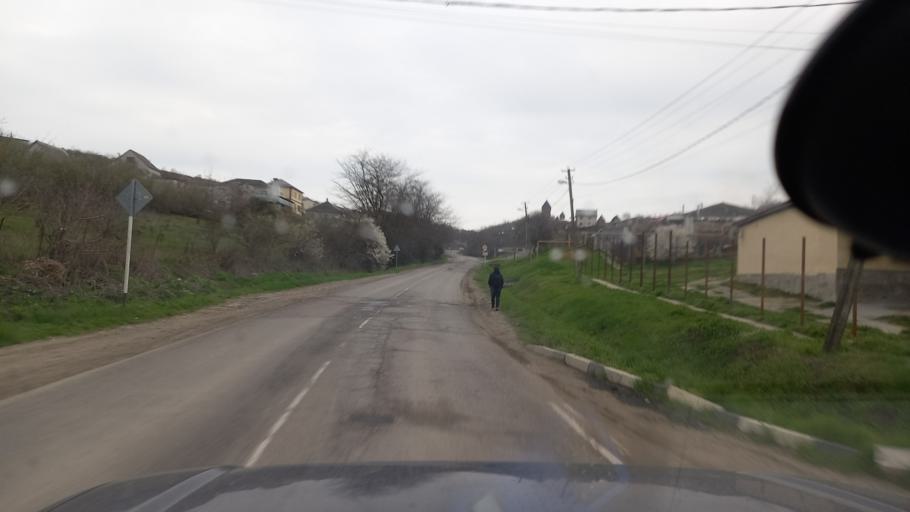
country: RU
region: Krasnodarskiy
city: Sukko
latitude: 44.8472
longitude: 37.4357
